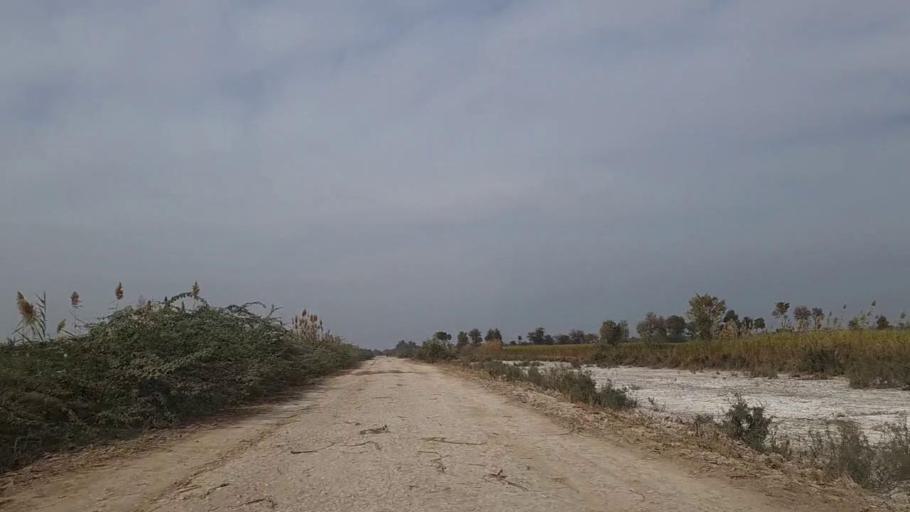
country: PK
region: Sindh
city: Daur
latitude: 26.4059
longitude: 68.4365
